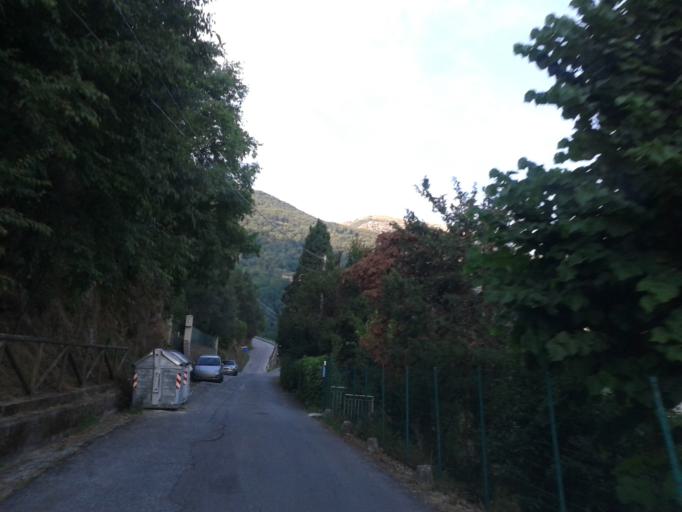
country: IT
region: Tuscany
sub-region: Provincia di Lucca
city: Pontestazzemese
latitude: 43.9611
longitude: 10.3274
